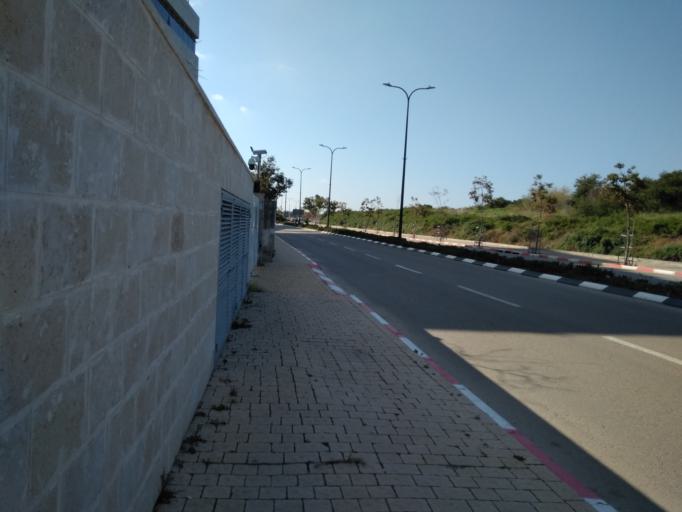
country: IL
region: Tel Aviv
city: Herzliya Pituah
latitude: 32.1623
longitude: 34.8058
